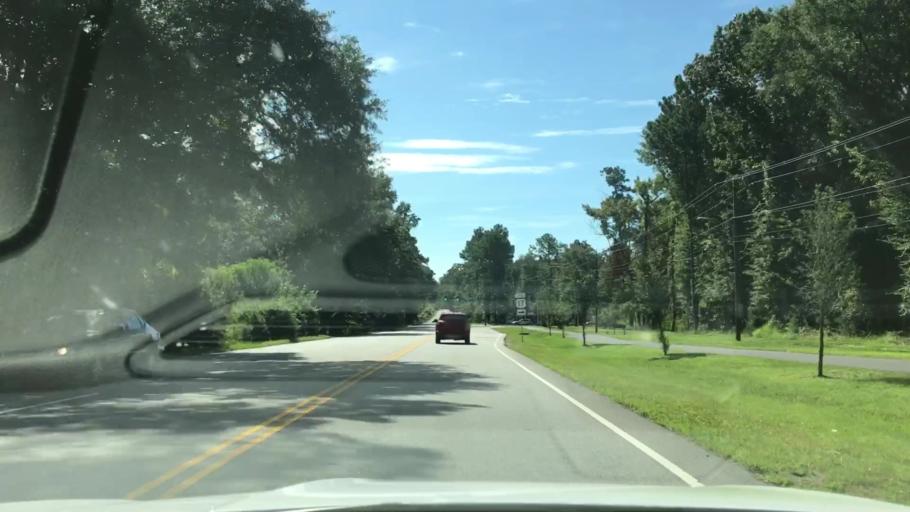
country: US
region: South Carolina
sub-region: Charleston County
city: Shell Point
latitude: 32.8454
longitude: -80.0604
